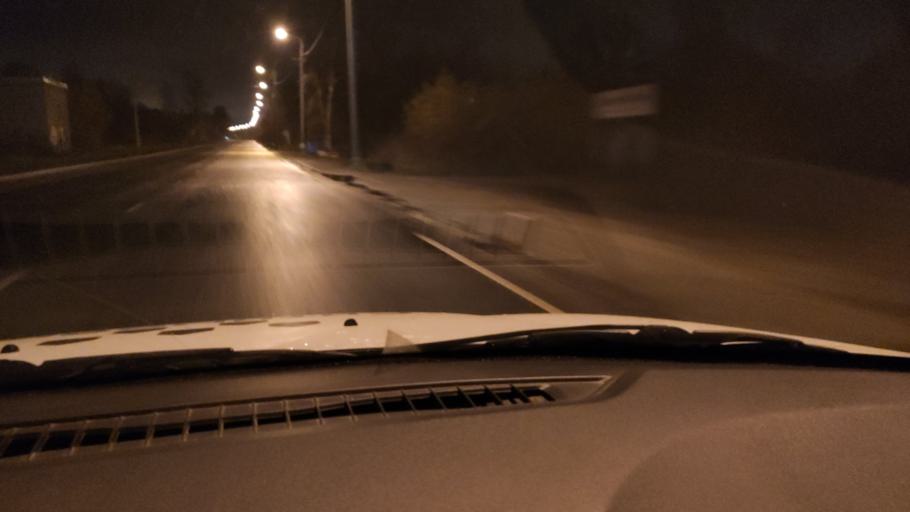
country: RU
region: Perm
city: Kondratovo
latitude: 57.9893
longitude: 56.1351
